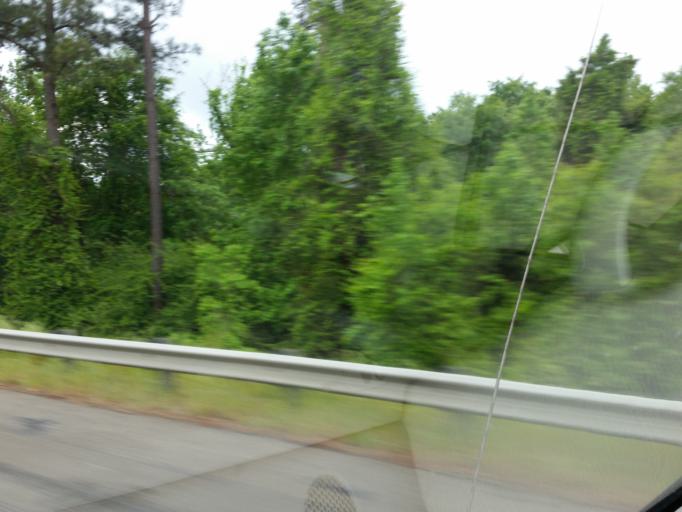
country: US
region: Georgia
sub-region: Houston County
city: Centerville
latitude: 32.5683
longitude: -83.7441
